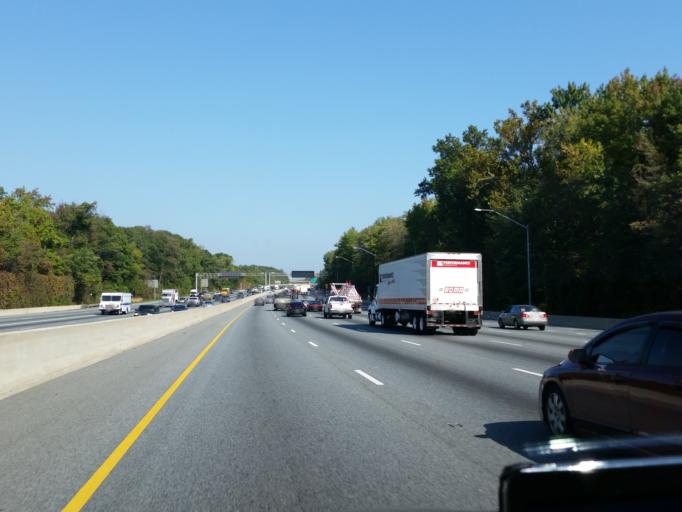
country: US
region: Maryland
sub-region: Prince George's County
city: Glenarden
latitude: 38.9239
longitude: -76.8535
